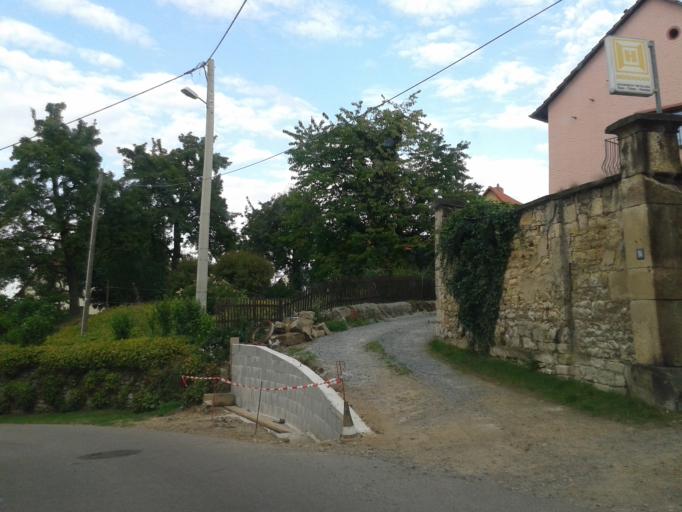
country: DE
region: Saxony
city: Bannewitz
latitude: 51.0023
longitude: 13.7318
